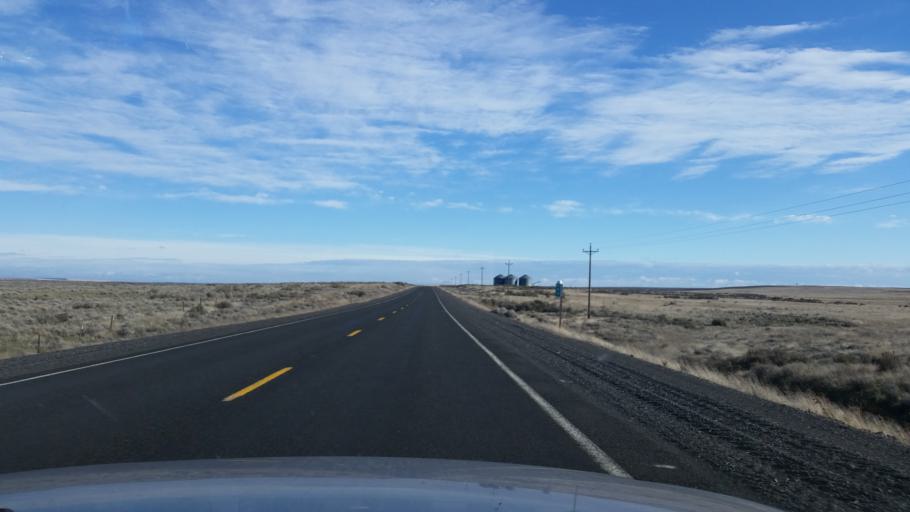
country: US
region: Washington
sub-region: Grant County
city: Warden
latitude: 47.3140
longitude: -118.7863
